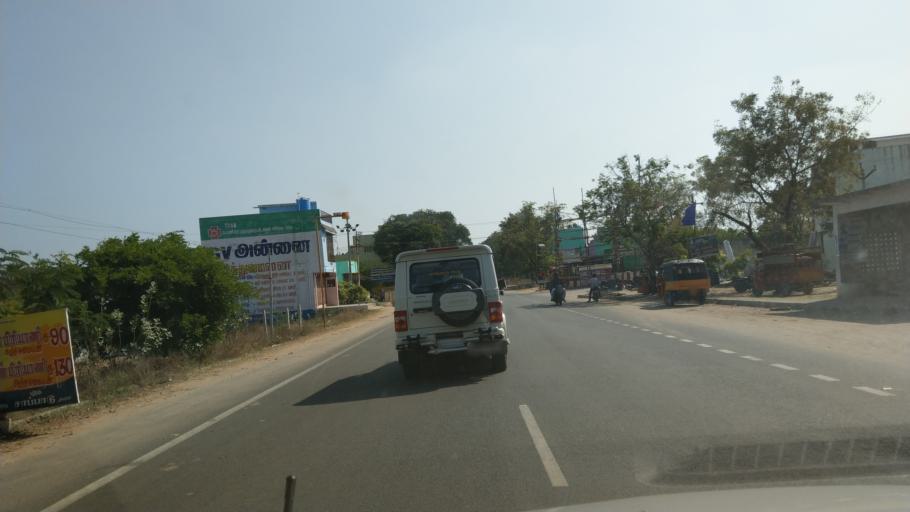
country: IN
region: Tamil Nadu
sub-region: Vellore
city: Arcot
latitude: 12.8899
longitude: 79.3191
